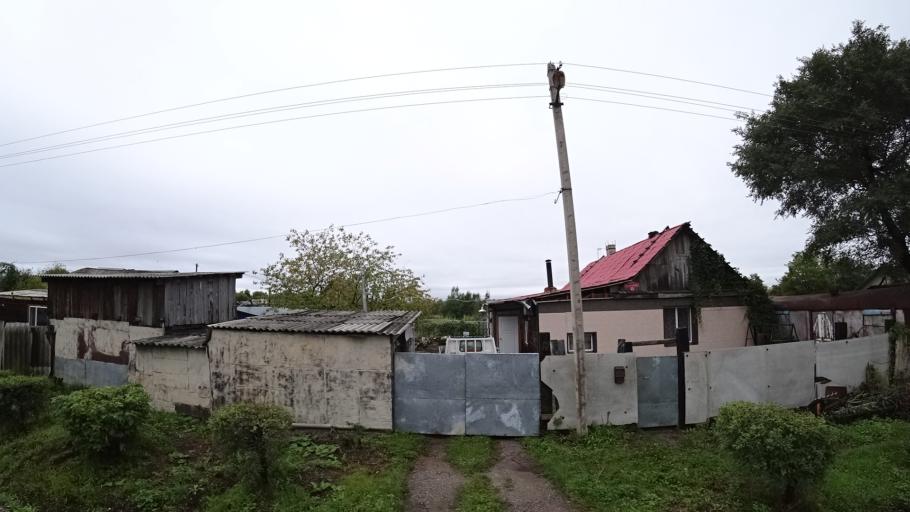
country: RU
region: Primorskiy
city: Monastyrishche
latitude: 44.1978
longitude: 132.4974
